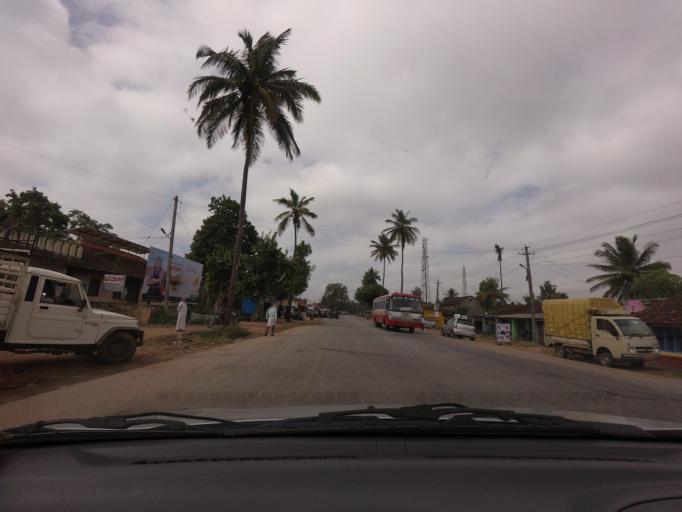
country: IN
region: Karnataka
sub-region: Hassan
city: Alur
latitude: 12.9499
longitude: 75.9410
